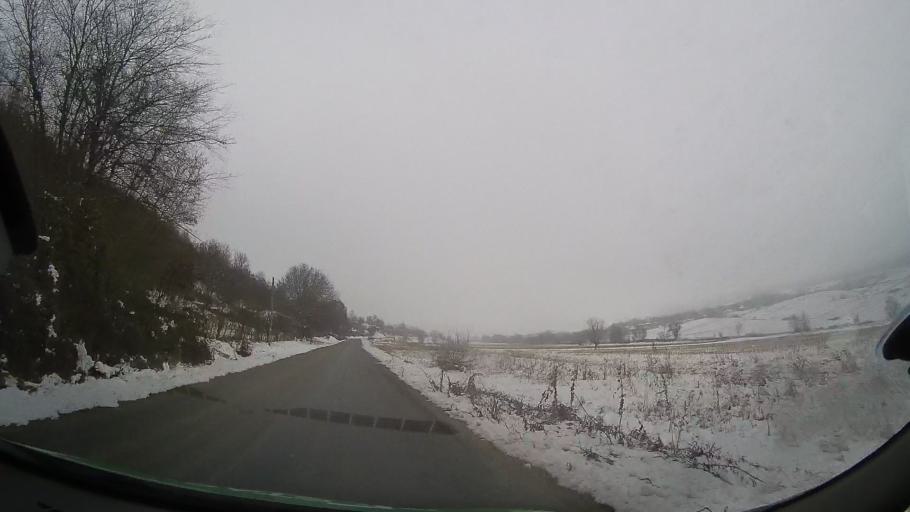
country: RO
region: Bacau
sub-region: Comuna Vultureni
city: Vultureni
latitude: 46.3359
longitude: 27.2909
